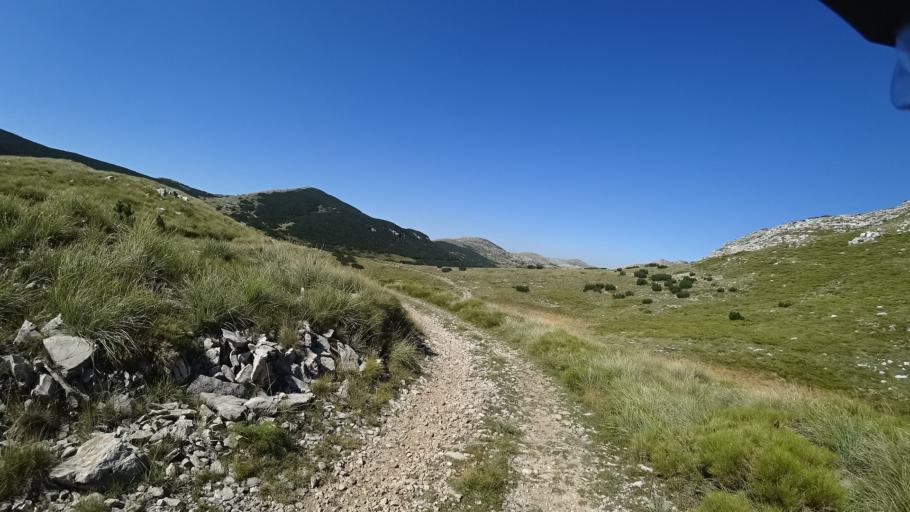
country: HR
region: Splitsko-Dalmatinska
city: Hrvace
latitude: 43.9409
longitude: 16.5837
